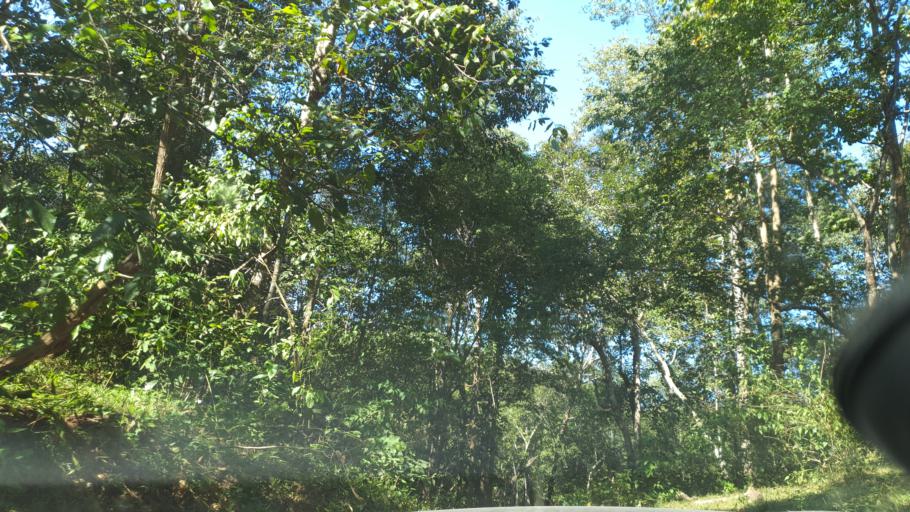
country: TH
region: Mae Hong Son
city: Mae Hi
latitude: 19.3028
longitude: 98.7003
